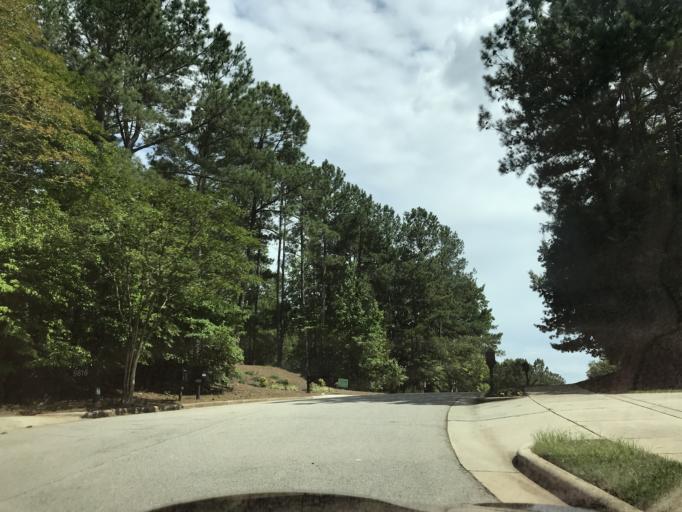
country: US
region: North Carolina
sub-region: Wake County
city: West Raleigh
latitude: 35.8663
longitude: -78.6960
